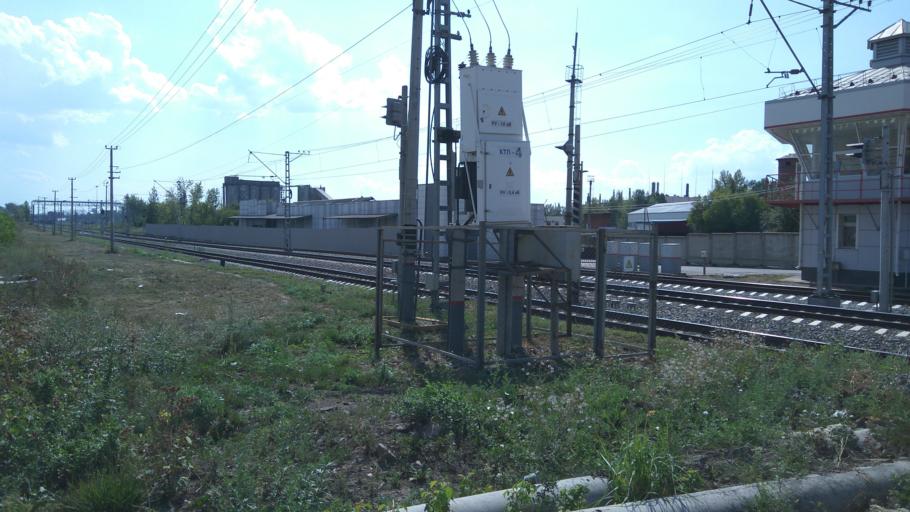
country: RU
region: Tatarstan
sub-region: Gorod Kazan'
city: Kazan
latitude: 55.7475
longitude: 49.1265
